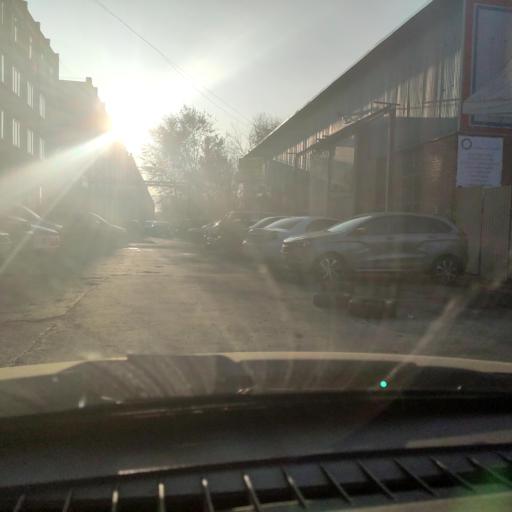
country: RU
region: Samara
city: Tol'yatti
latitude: 53.5418
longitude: 49.3120
